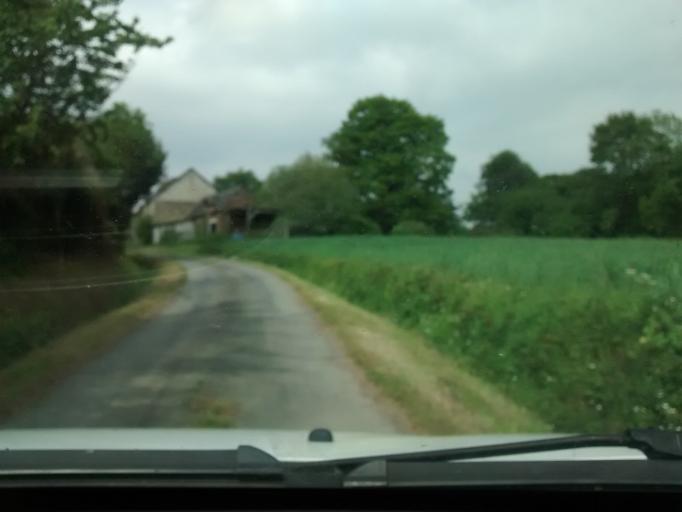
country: FR
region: Brittany
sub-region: Departement d'Ille-et-Vilaine
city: La Dominelais
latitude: 47.7737
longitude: -1.7359
